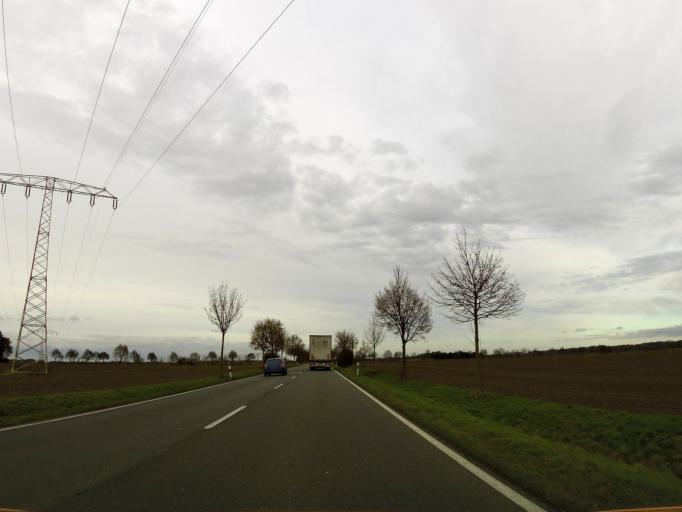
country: DE
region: Saxony-Anhalt
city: Pretzier
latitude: 52.7795
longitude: 11.2340
